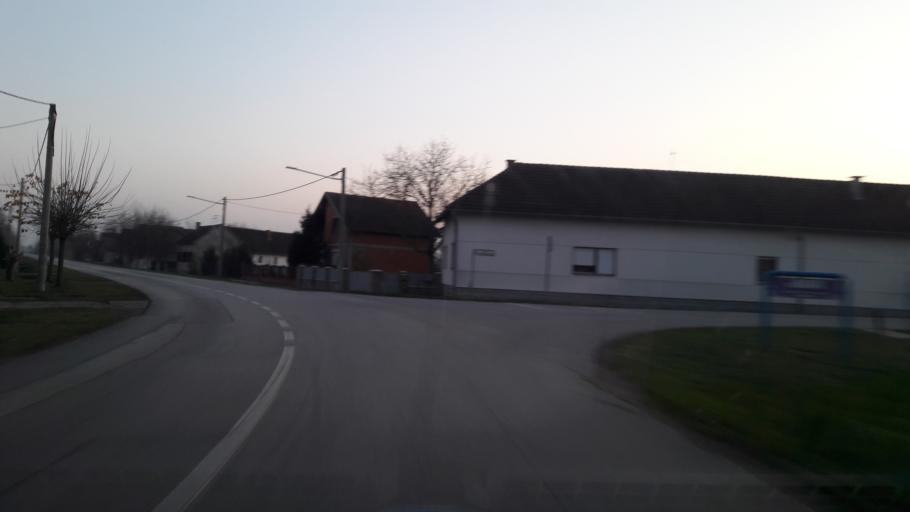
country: HR
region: Vukovarsko-Srijemska
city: Nijemci
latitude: 45.1794
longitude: 19.0114
